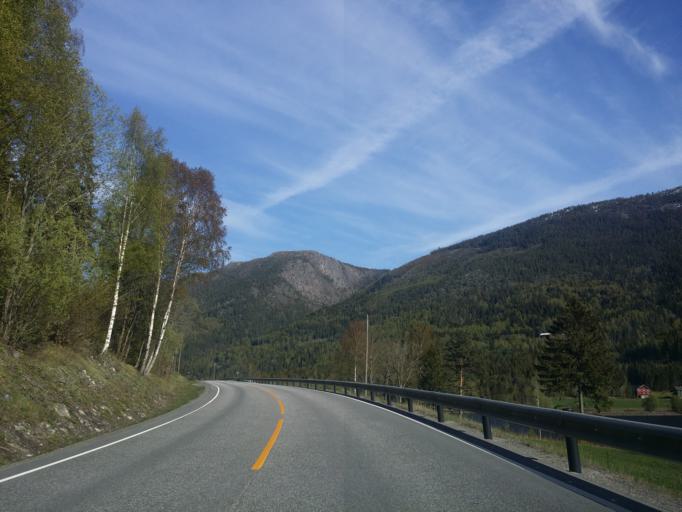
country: NO
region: Telemark
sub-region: Seljord
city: Seljord
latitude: 59.6095
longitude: 8.7571
